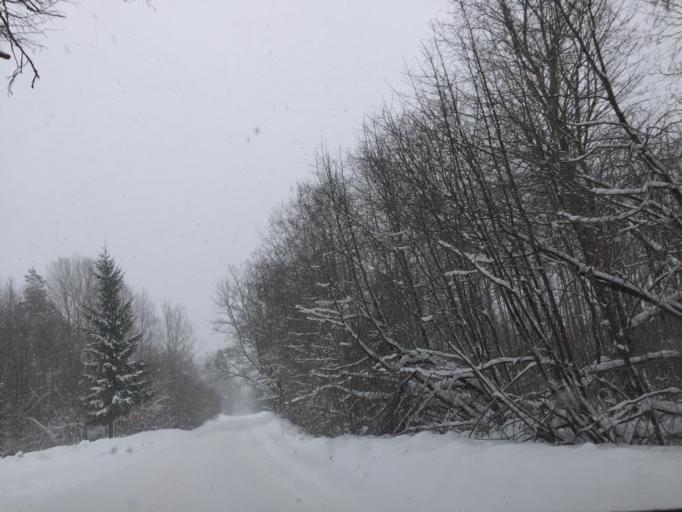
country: LV
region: Amatas Novads
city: Drabesi
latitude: 57.0859
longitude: 25.3594
